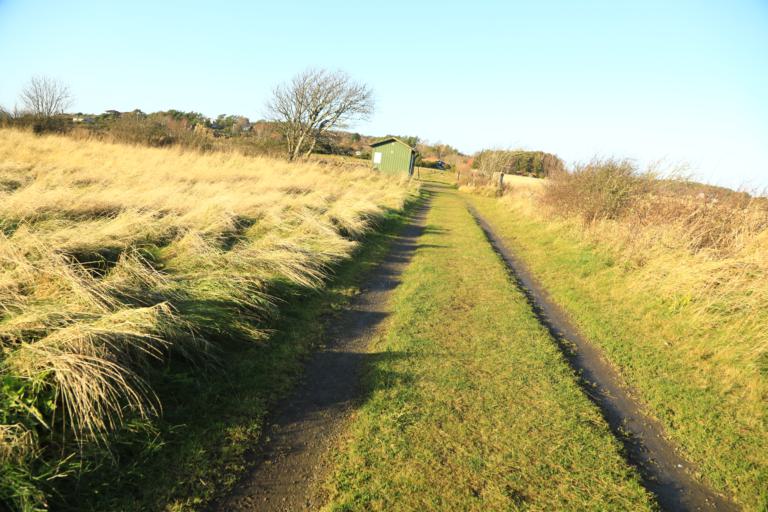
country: SE
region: Halland
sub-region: Varbergs Kommun
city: Varberg
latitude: 57.1663
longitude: 12.2220
